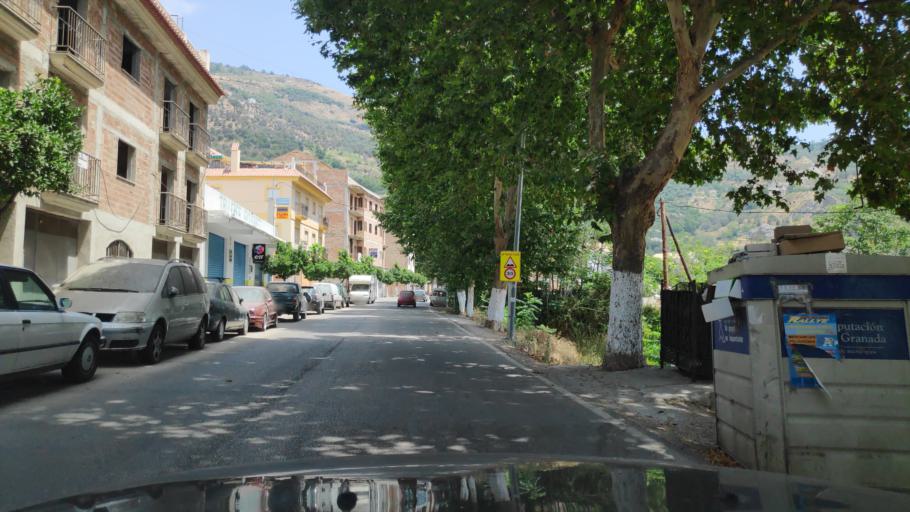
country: ES
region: Andalusia
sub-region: Provincia de Granada
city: Lanjaron
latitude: 36.9194
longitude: -3.4755
